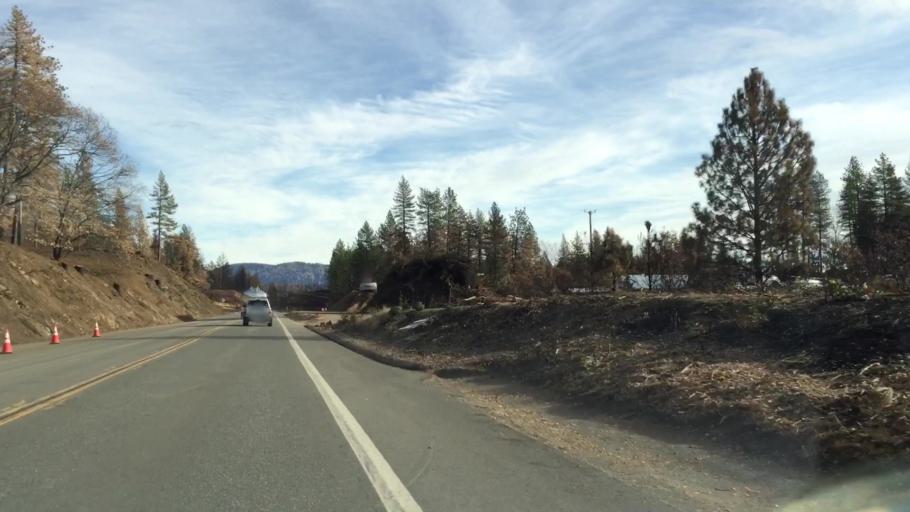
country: US
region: California
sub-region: Butte County
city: Magalia
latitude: 39.7187
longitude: -121.5180
